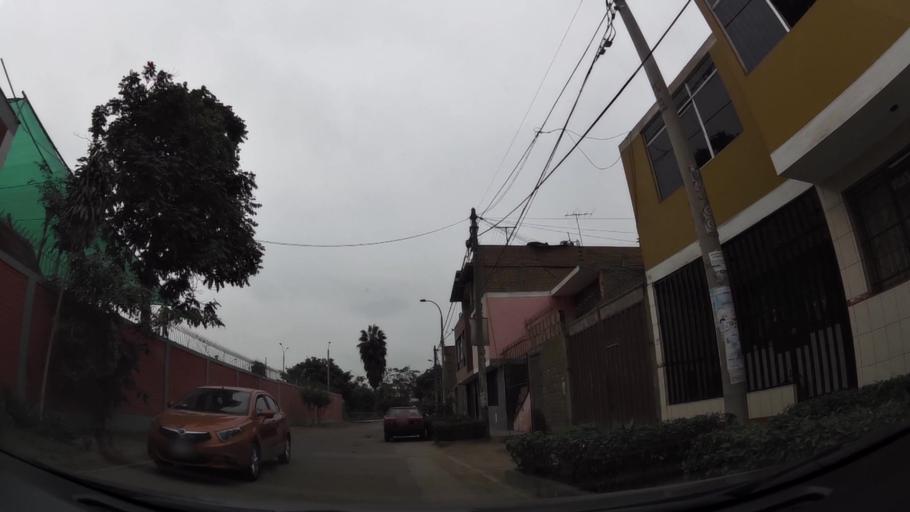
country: PE
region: Lima
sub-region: Lima
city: Independencia
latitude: -11.9639
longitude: -77.0608
